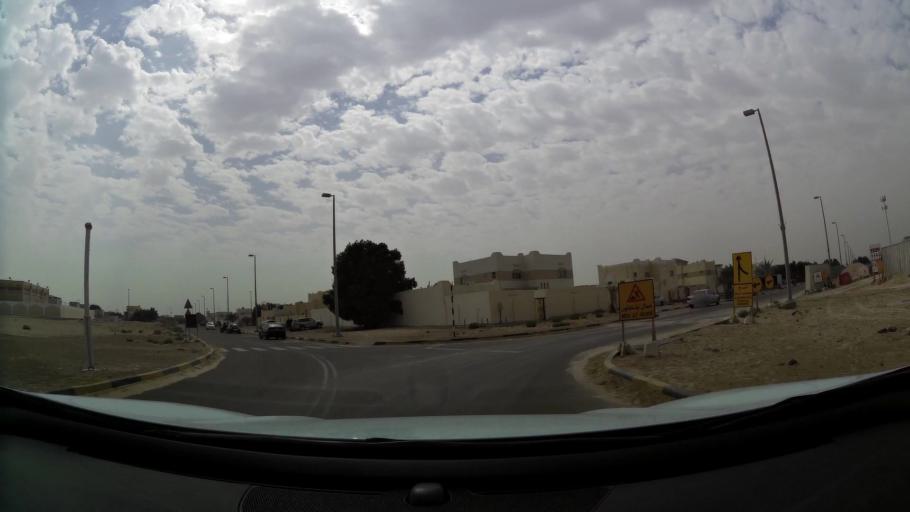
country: AE
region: Abu Dhabi
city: Abu Dhabi
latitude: 24.3153
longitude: 54.6321
